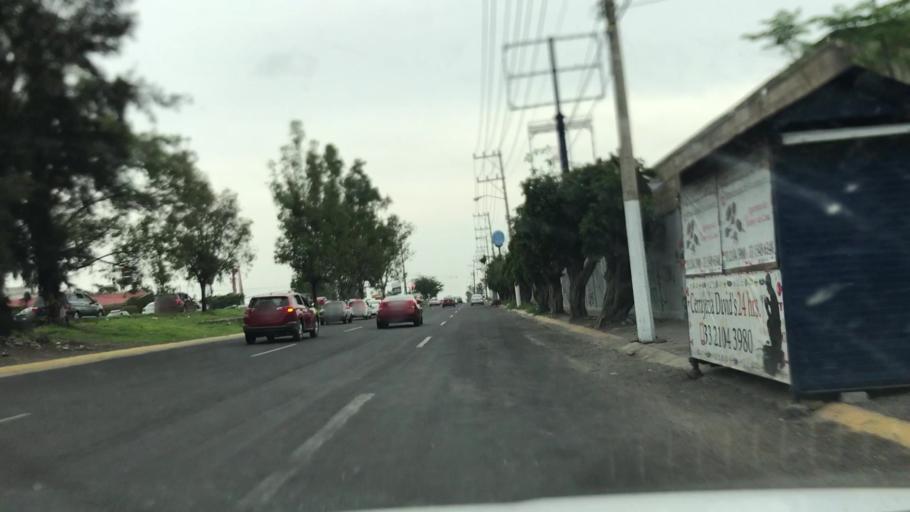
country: MX
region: Jalisco
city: Nuevo Mexico
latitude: 20.7485
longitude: -103.4178
